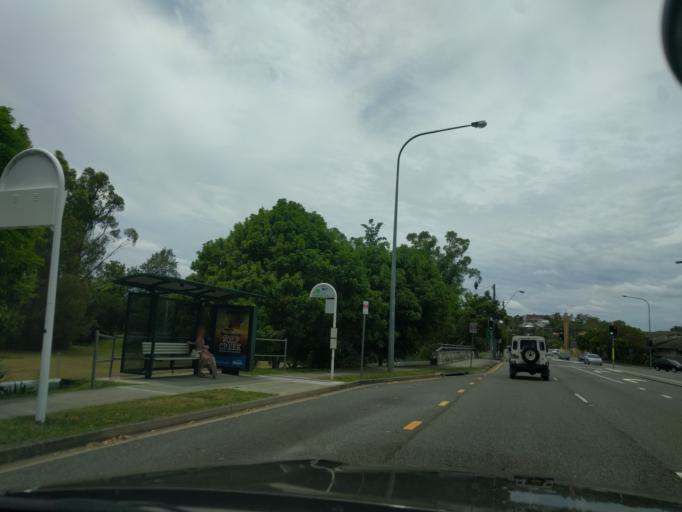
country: AU
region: Queensland
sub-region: Brisbane
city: Stafford
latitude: -27.4177
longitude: 153.0000
